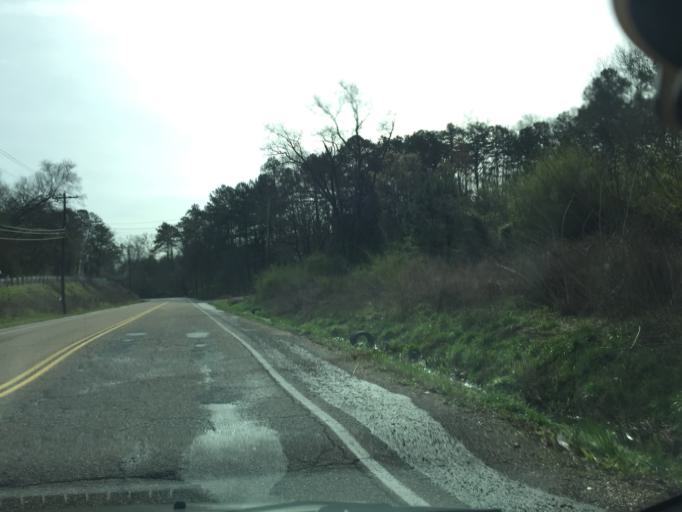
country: US
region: Tennessee
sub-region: Hamilton County
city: Harrison
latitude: 35.0697
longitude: -85.1060
